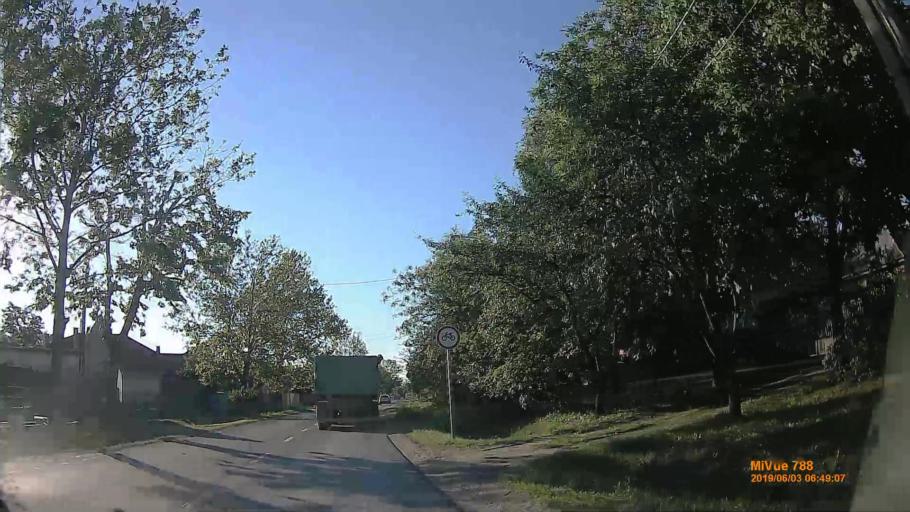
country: HU
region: Pest
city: Bugyi
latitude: 47.2213
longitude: 19.1619
